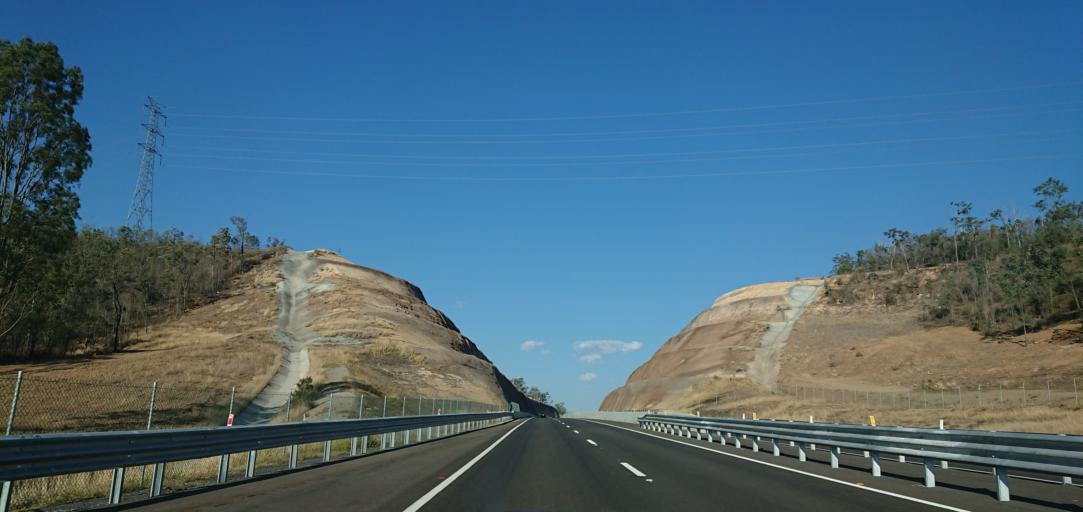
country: AU
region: Queensland
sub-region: Toowoomba
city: East Toowoomba
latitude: -27.5147
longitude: 152.0376
